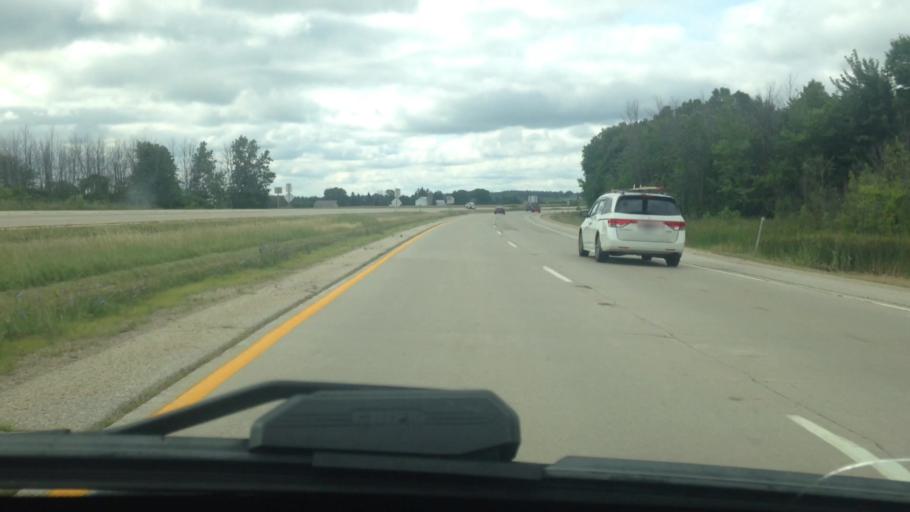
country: US
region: Wisconsin
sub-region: Washington County
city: Jackson
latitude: 43.3188
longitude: -88.1849
